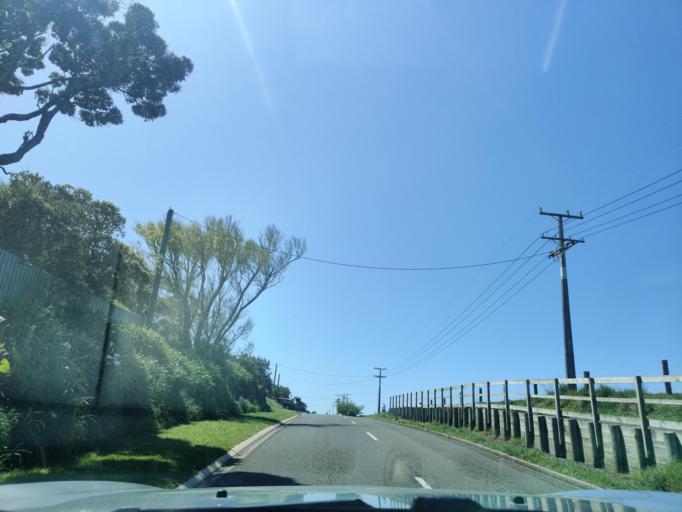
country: NZ
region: Taranaki
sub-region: South Taranaki District
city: Hawera
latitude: -39.6011
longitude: 174.2618
